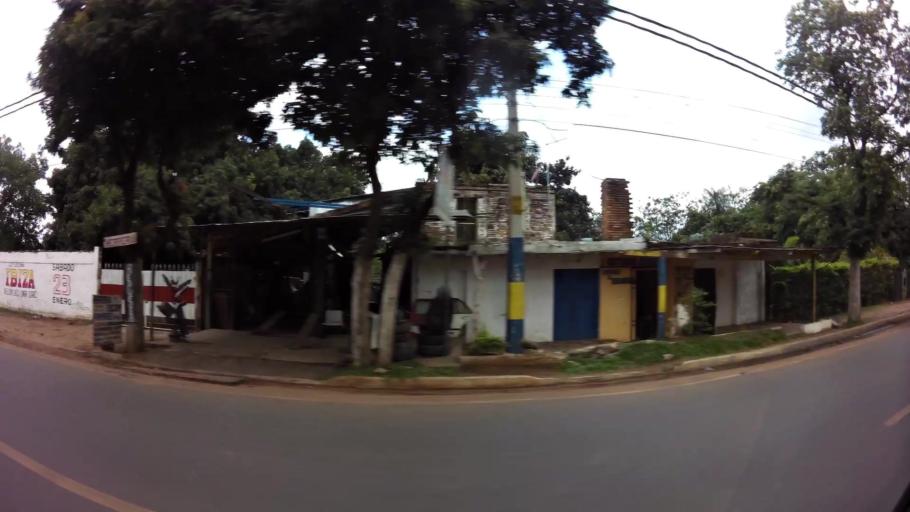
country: PY
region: Central
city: San Lorenzo
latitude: -25.2862
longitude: -57.4828
